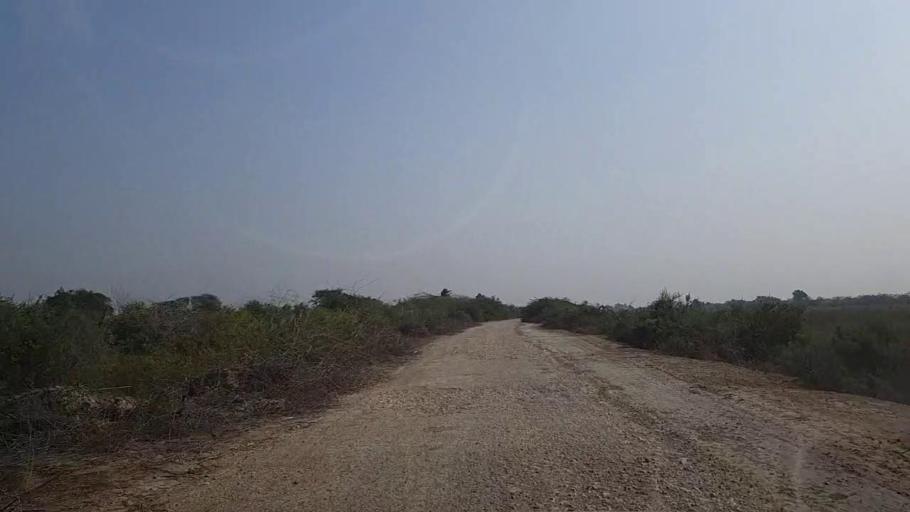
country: PK
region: Sindh
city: Keti Bandar
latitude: 24.2510
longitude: 67.6292
